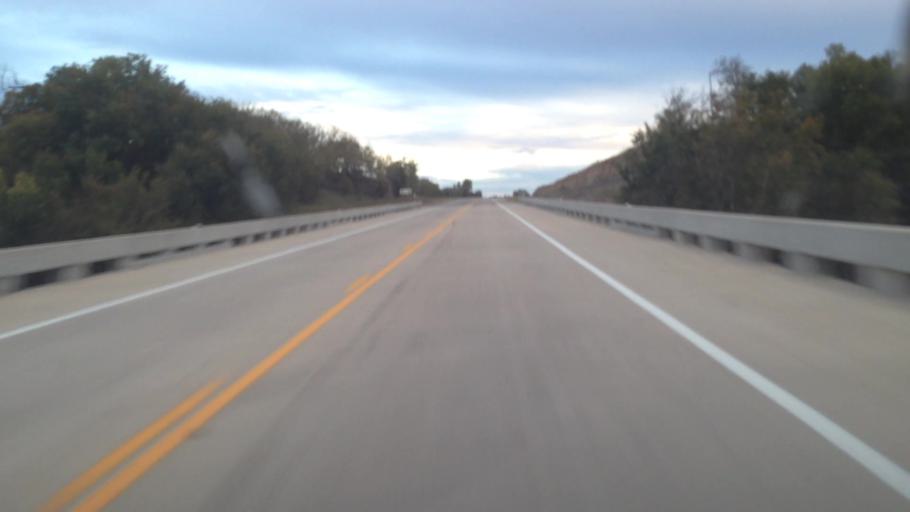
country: US
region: Kansas
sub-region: Anderson County
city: Garnett
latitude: 38.3344
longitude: -95.2491
